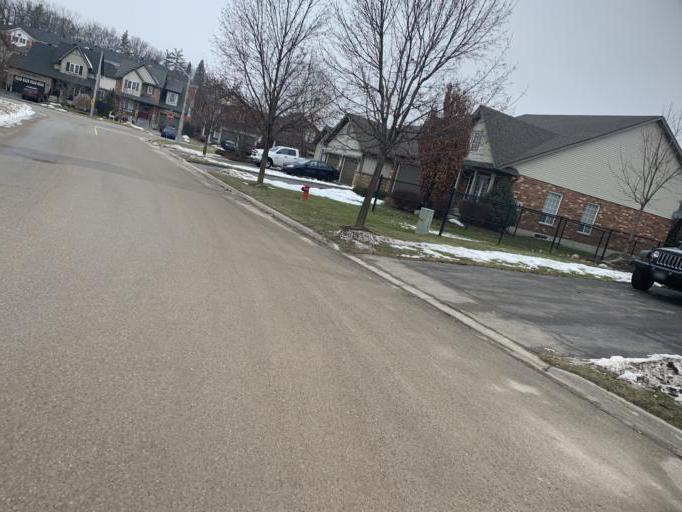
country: CA
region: Ontario
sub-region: Halton
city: Milton
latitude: 43.6602
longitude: -79.9188
